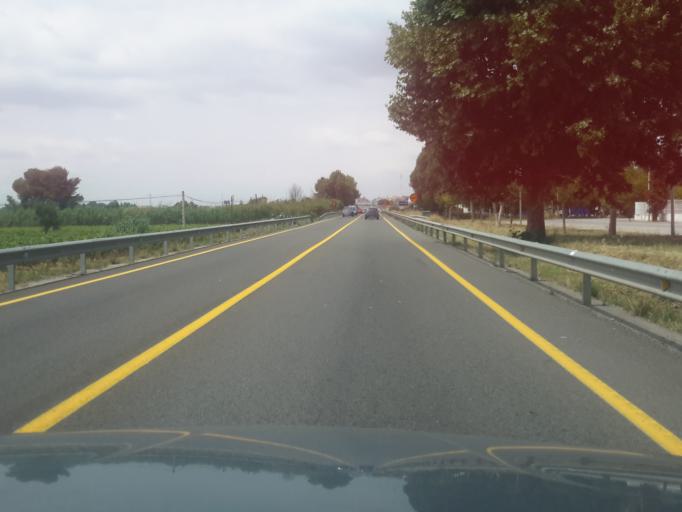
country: ES
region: Catalonia
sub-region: Provincia de Barcelona
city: La Granada
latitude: 41.3523
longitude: 1.7298
